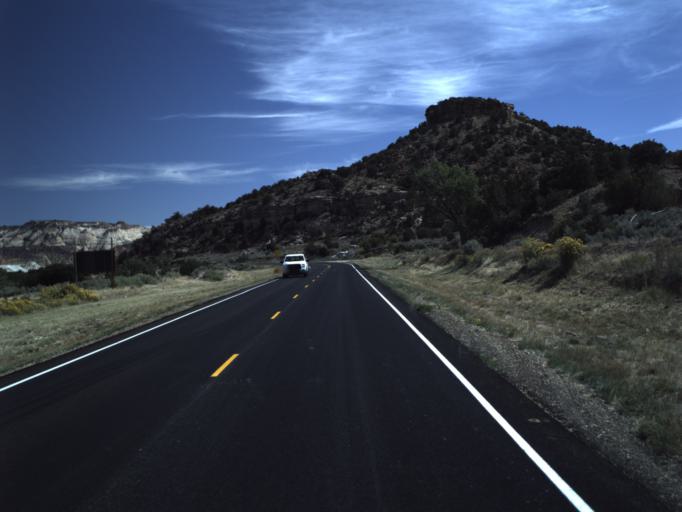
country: US
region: Utah
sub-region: Wayne County
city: Loa
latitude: 37.7759
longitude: -111.6355
